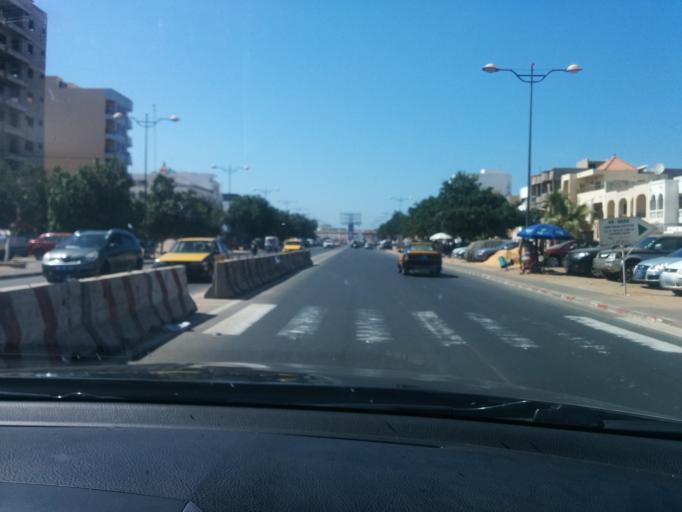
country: SN
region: Dakar
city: Mermoz Boabab
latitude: 14.7169
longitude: -17.4685
